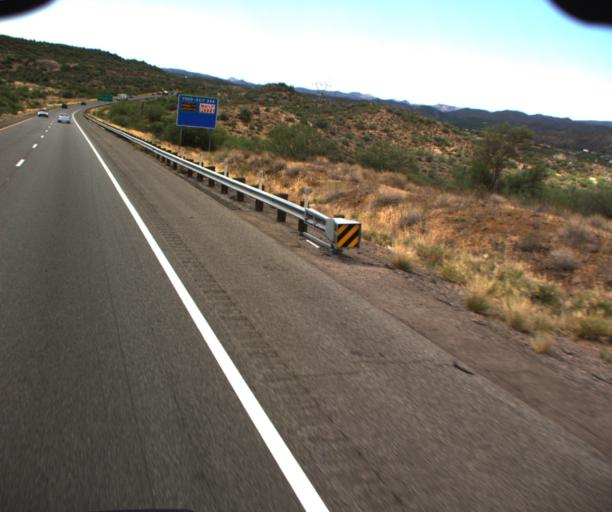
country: US
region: Arizona
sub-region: Yavapai County
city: Black Canyon City
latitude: 34.1060
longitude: -112.1441
